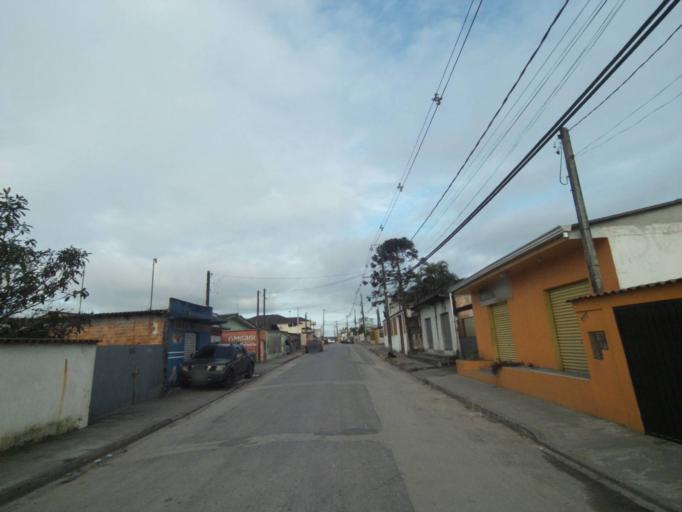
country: BR
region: Parana
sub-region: Paranagua
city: Paranagua
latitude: -25.5309
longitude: -48.5482
